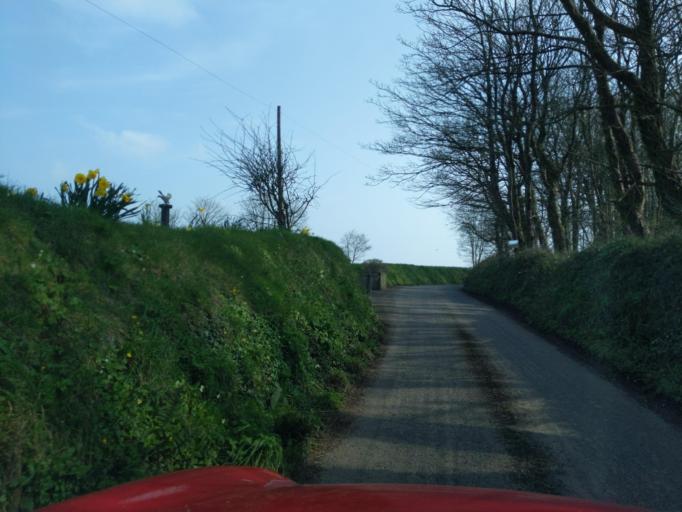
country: GB
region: England
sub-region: Devon
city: Kingsbridge
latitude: 50.3092
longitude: -3.7696
